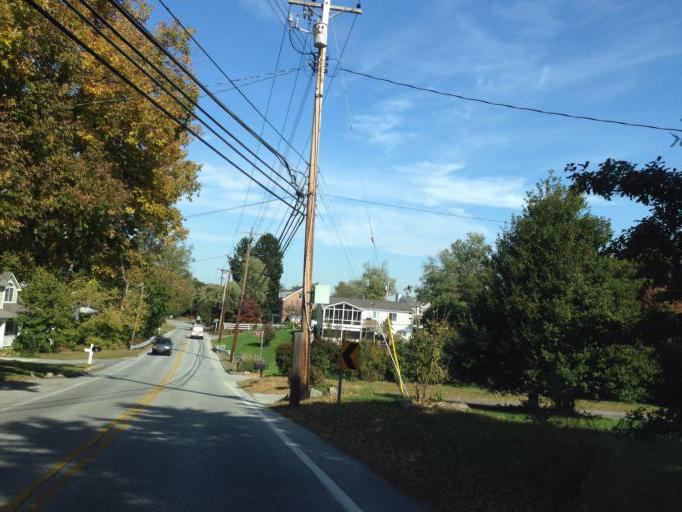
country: US
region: Maryland
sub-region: Howard County
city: Ellicott City
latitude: 39.2632
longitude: -76.8065
